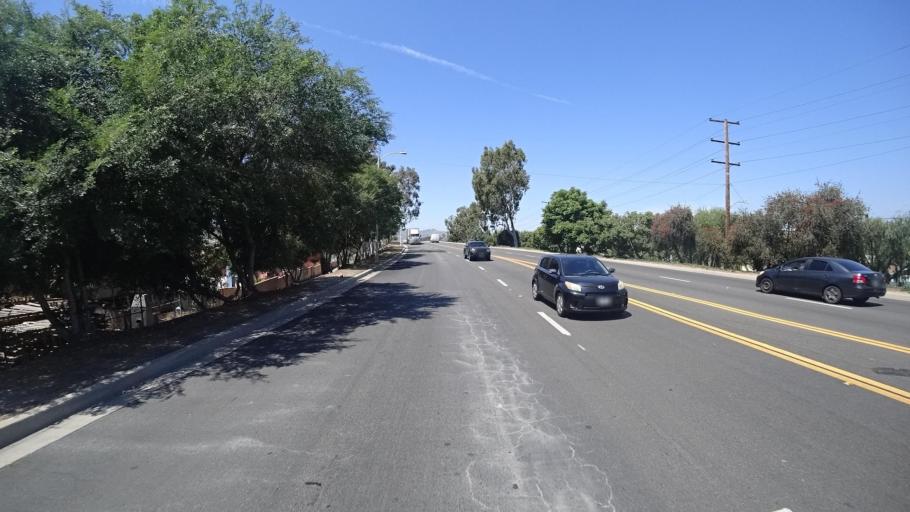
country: US
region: California
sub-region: Los Angeles County
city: La Puente
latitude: 34.0153
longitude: -117.9459
